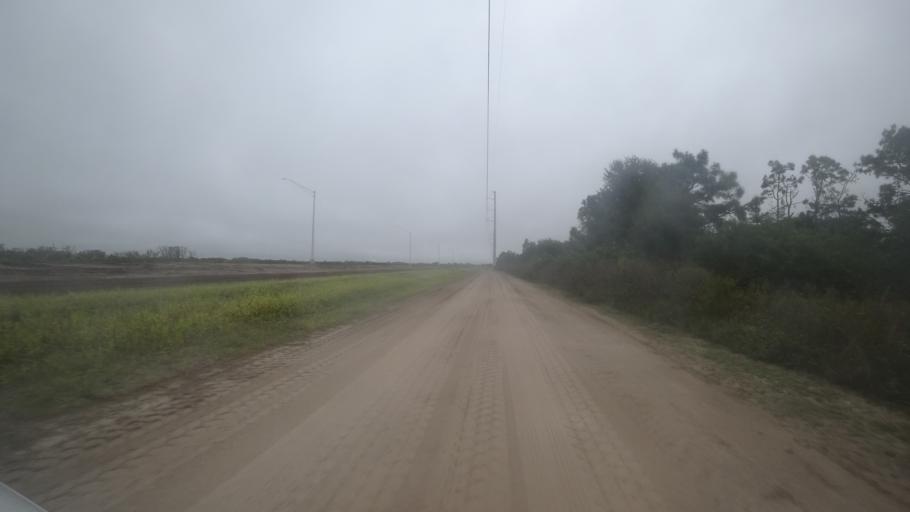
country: US
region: Florida
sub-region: Sarasota County
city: The Meadows
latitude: 27.4642
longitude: -82.3507
